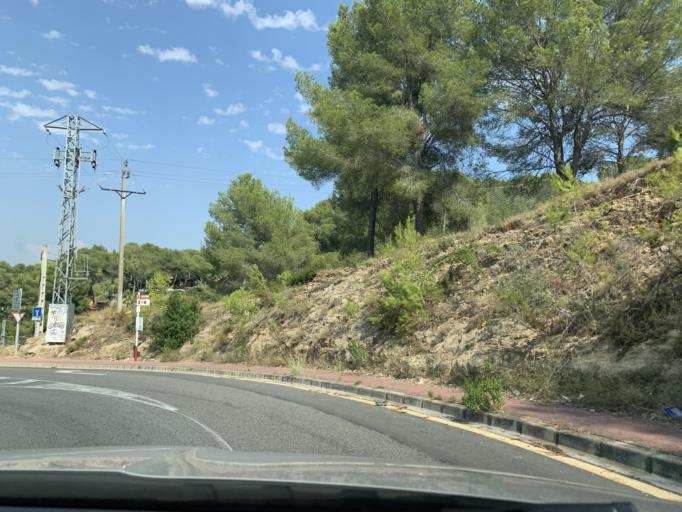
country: ES
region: Catalonia
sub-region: Provincia de Tarragona
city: Altafulla
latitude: 41.1383
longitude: 1.3531
